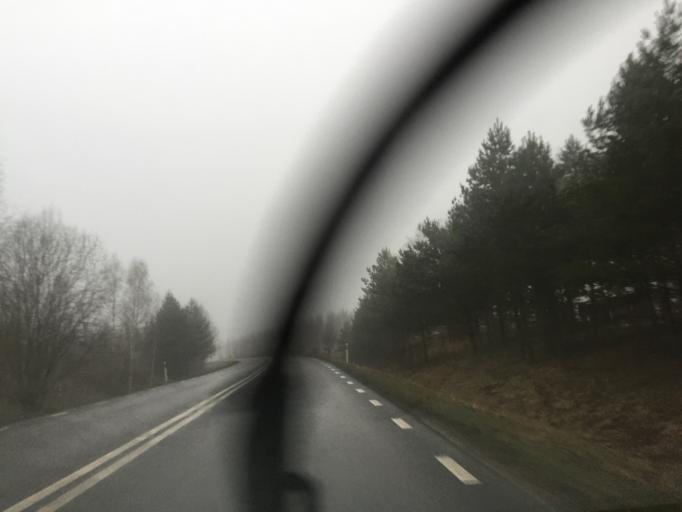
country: SE
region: Soedermanland
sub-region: Katrineholms Kommun
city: Katrineholm
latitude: 58.9330
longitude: 16.4073
